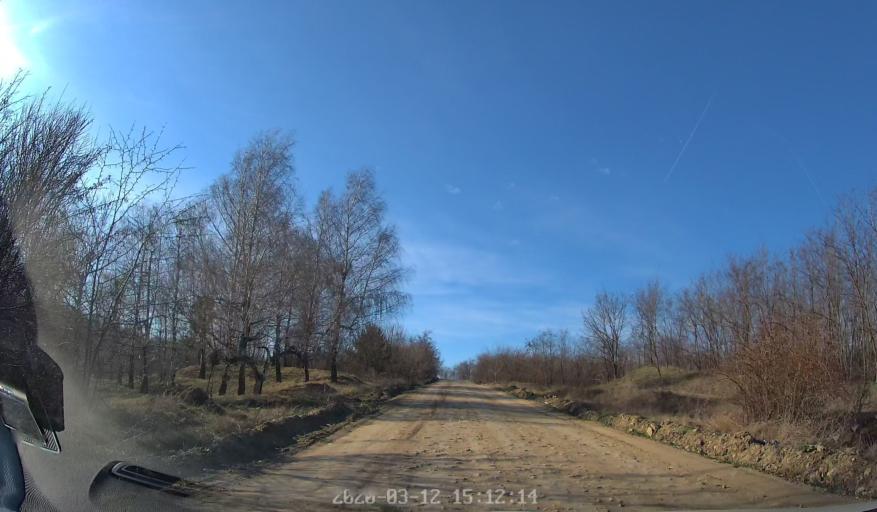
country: MD
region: Chisinau
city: Ciorescu
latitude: 47.2286
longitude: 28.9721
